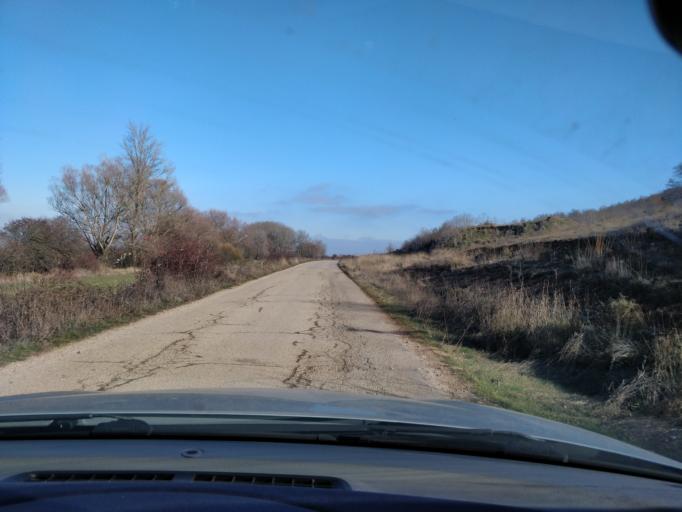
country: ES
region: Castille and Leon
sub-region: Provincia de Burgos
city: Quintanaortuno
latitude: 42.5178
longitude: -3.6869
